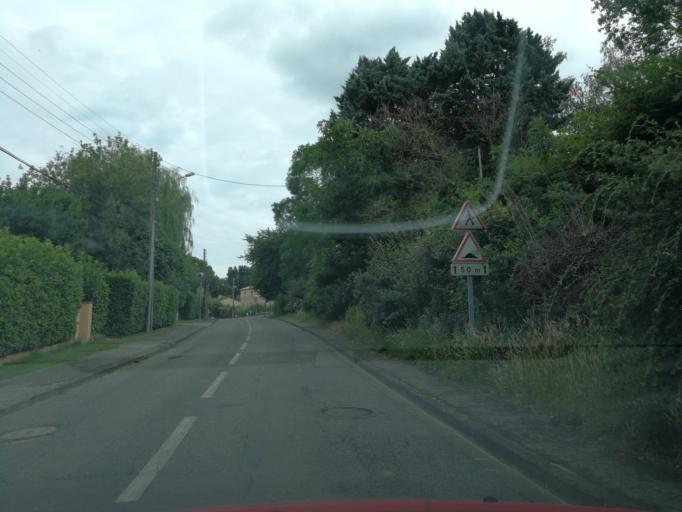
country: FR
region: Midi-Pyrenees
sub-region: Departement de la Haute-Garonne
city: Auzeville-Tolosane
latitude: 43.5273
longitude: 1.4826
